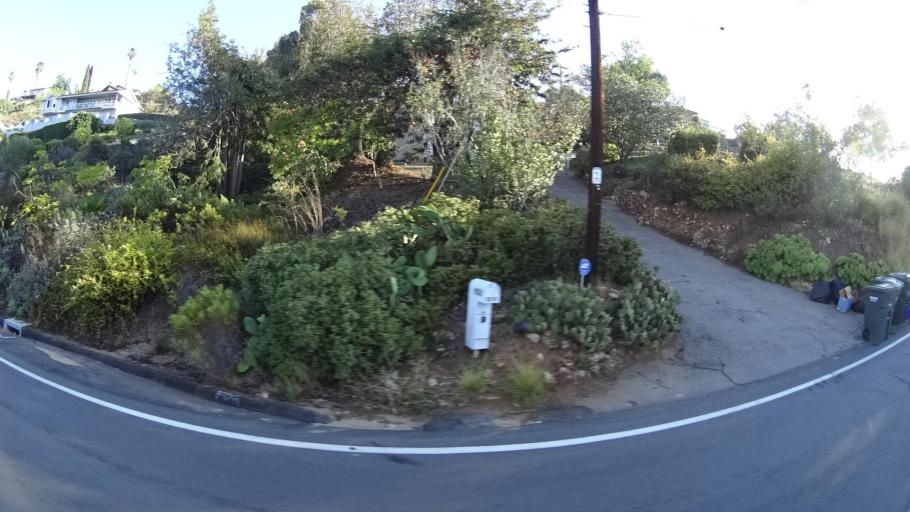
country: US
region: California
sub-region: San Diego County
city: Spring Valley
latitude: 32.7600
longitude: -116.9971
